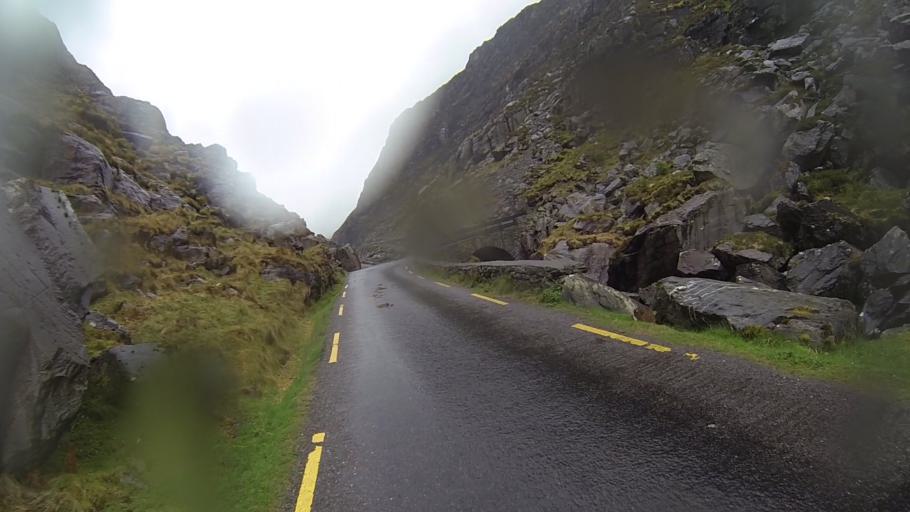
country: IE
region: Munster
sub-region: Ciarrai
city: Cill Airne
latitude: 52.0074
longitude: -9.6417
